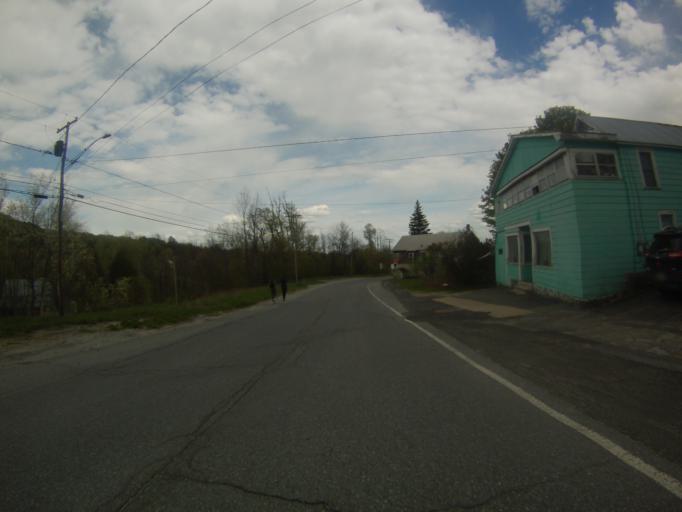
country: US
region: New York
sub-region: Essex County
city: Mineville
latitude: 44.0879
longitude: -73.5350
